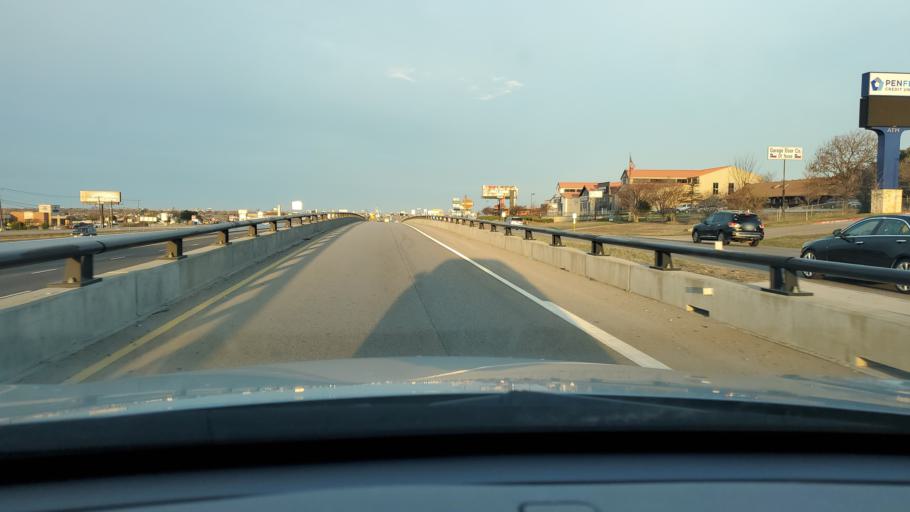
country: US
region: Texas
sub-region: Bell County
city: Harker Heights
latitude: 31.0744
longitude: -97.6817
